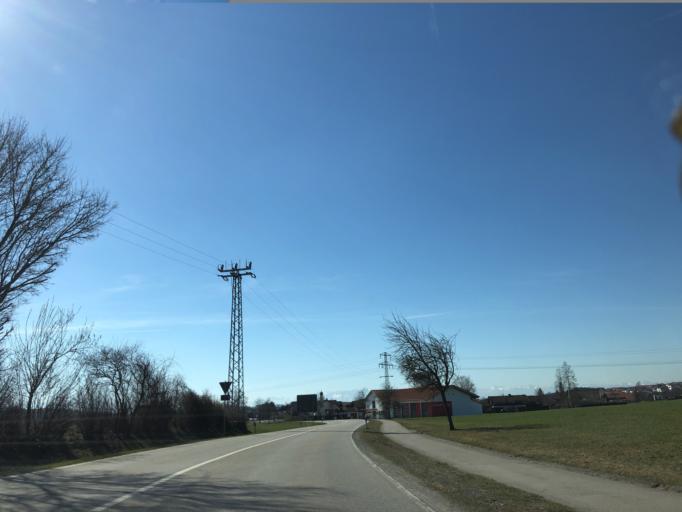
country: DE
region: Bavaria
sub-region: Upper Bavaria
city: Pfaffing
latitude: 48.0615
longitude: 12.1111
